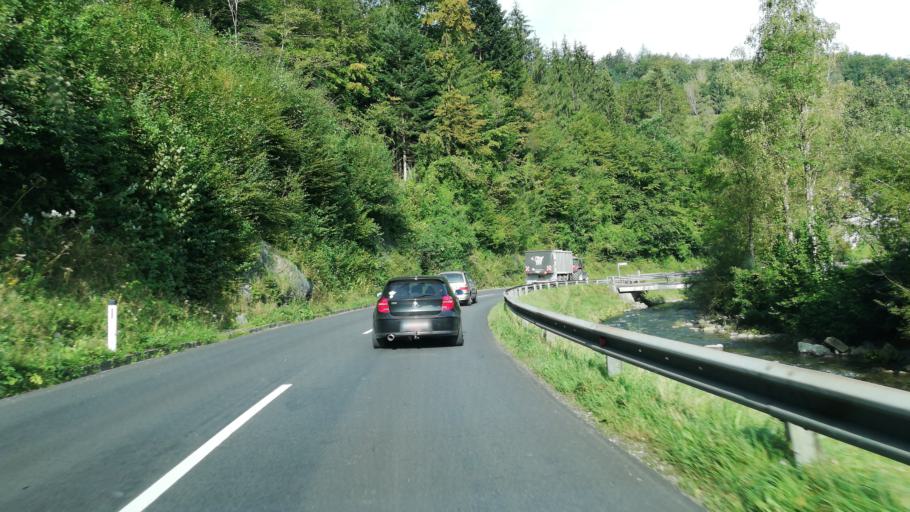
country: AT
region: Lower Austria
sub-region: Politischer Bezirk Amstetten
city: Behamberg
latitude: 47.9976
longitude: 14.4936
